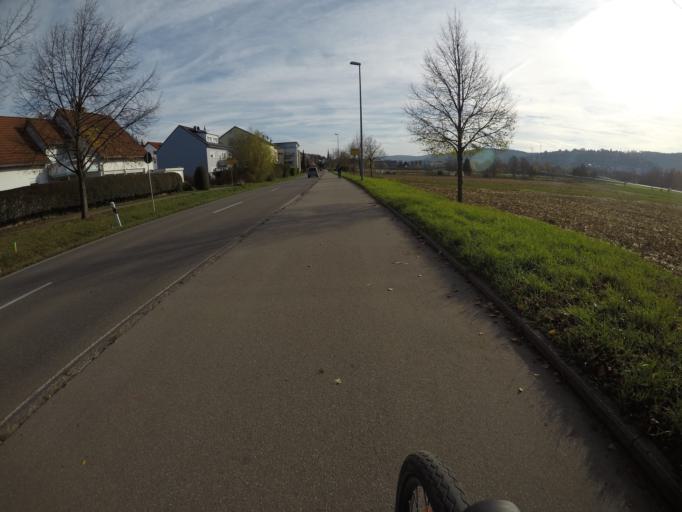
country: DE
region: Baden-Wuerttemberg
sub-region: Regierungsbezirk Stuttgart
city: Winterbach
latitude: 48.8137
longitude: 9.4303
